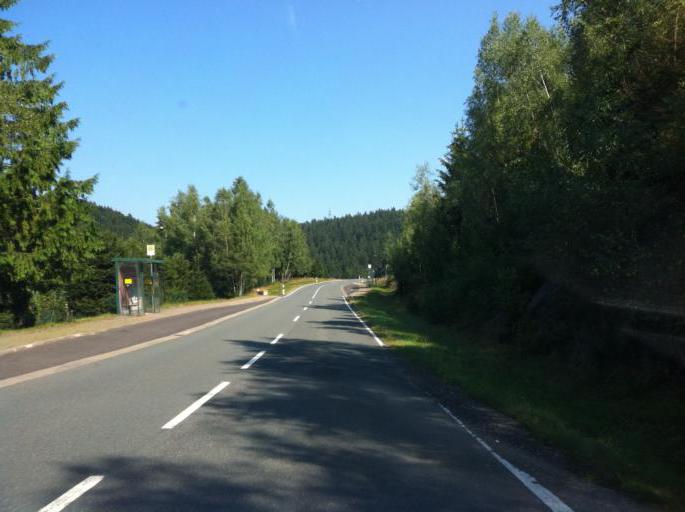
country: DE
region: Thuringia
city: Goldisthal
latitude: 50.5197
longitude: 11.0083
